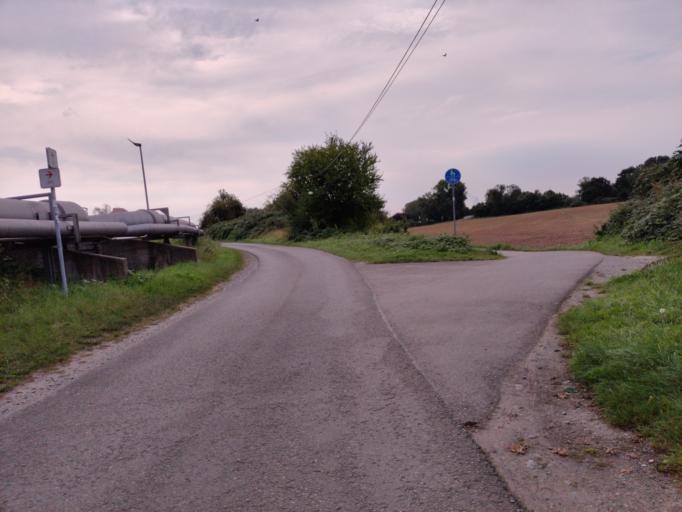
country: DE
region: Lower Saxony
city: Hameln
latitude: 52.0929
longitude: 9.3600
